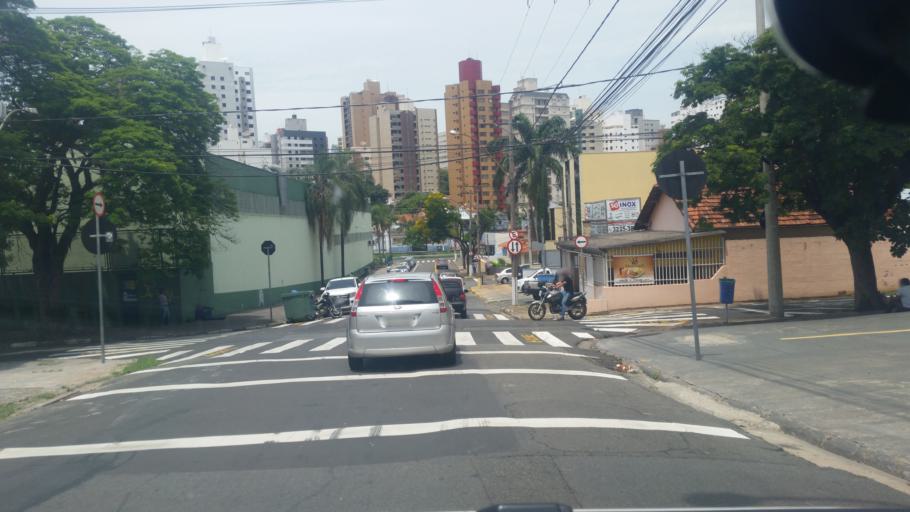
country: BR
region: Sao Paulo
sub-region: Campinas
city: Campinas
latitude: -22.8897
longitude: -47.0596
